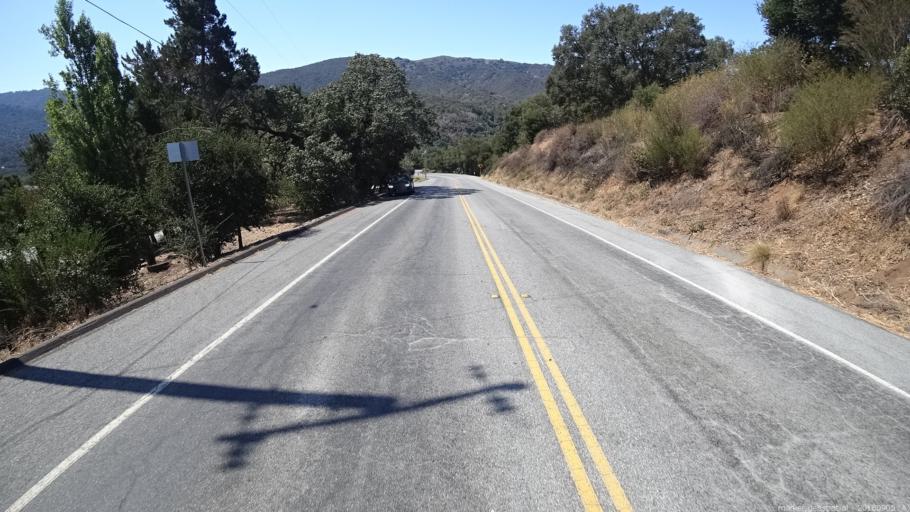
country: US
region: California
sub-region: Monterey County
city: Carmel Valley Village
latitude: 36.5021
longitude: -121.7544
